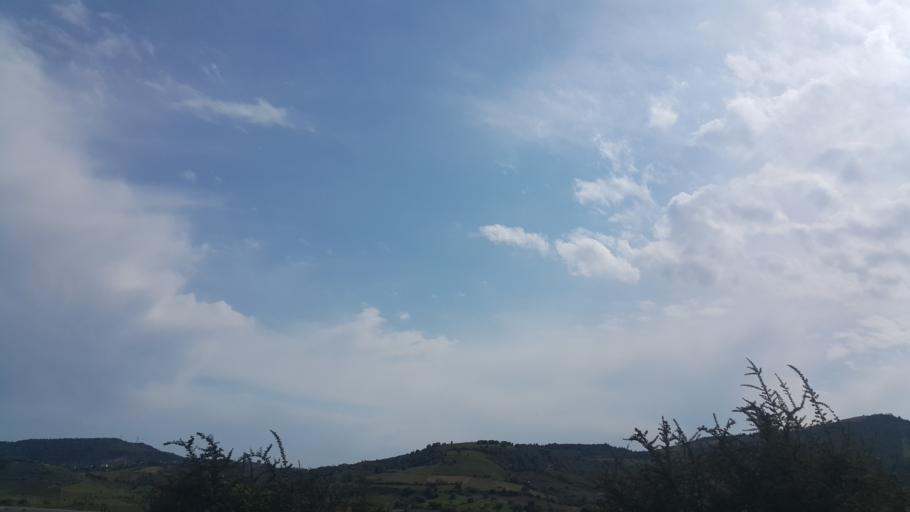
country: TR
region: Mersin
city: Tarsus
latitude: 36.9513
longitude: 34.7726
